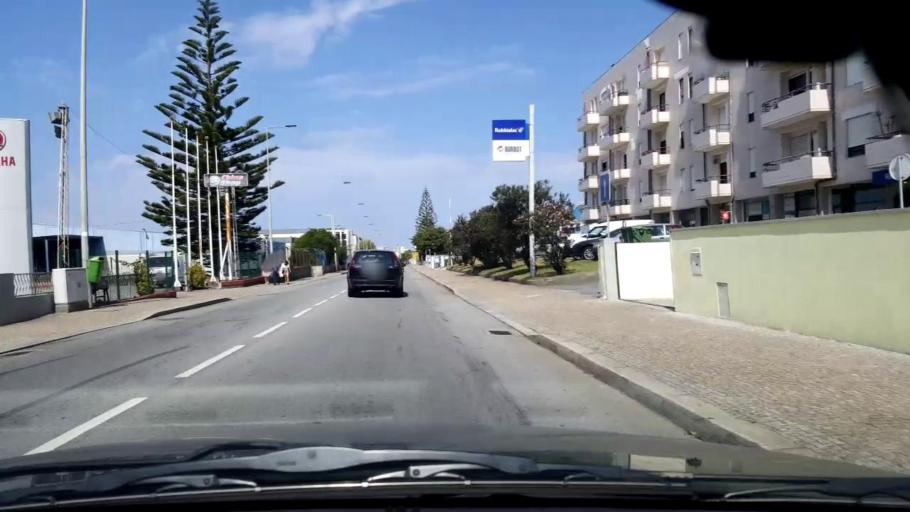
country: PT
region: Porto
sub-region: Vila do Conde
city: Vila do Conde
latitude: 41.3650
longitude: -8.7484
